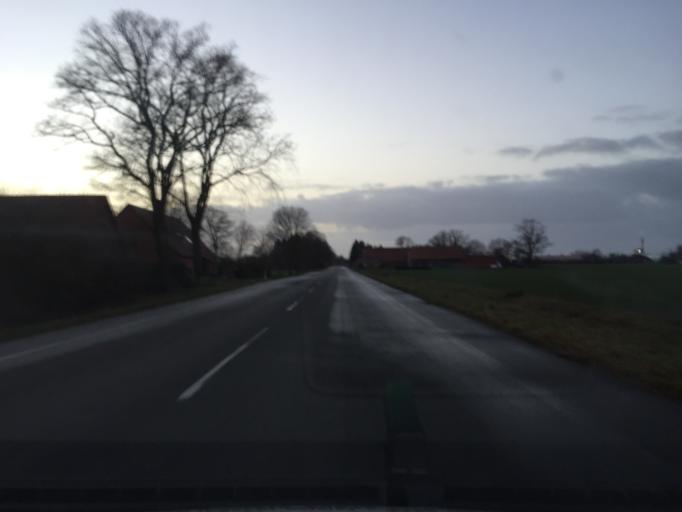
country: DE
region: Lower Saxony
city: Hassel
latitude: 52.6847
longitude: 8.8469
